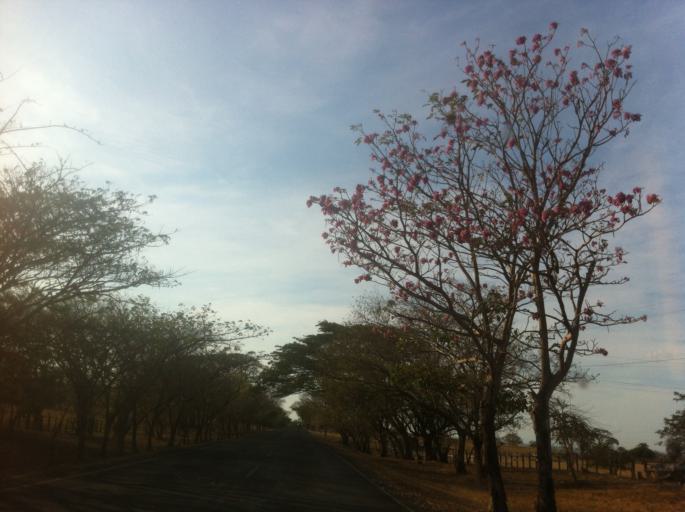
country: NI
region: Rivas
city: Cardenas
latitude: 11.2677
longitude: -85.6478
